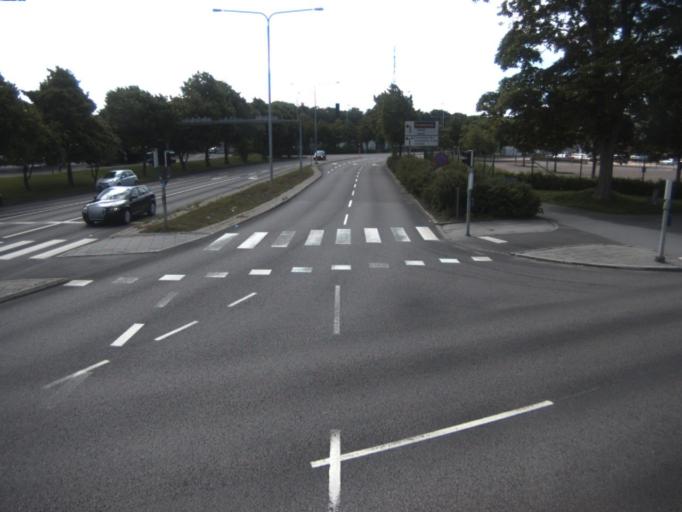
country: SE
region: Skane
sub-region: Helsingborg
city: Helsingborg
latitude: 56.0584
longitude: 12.7039
